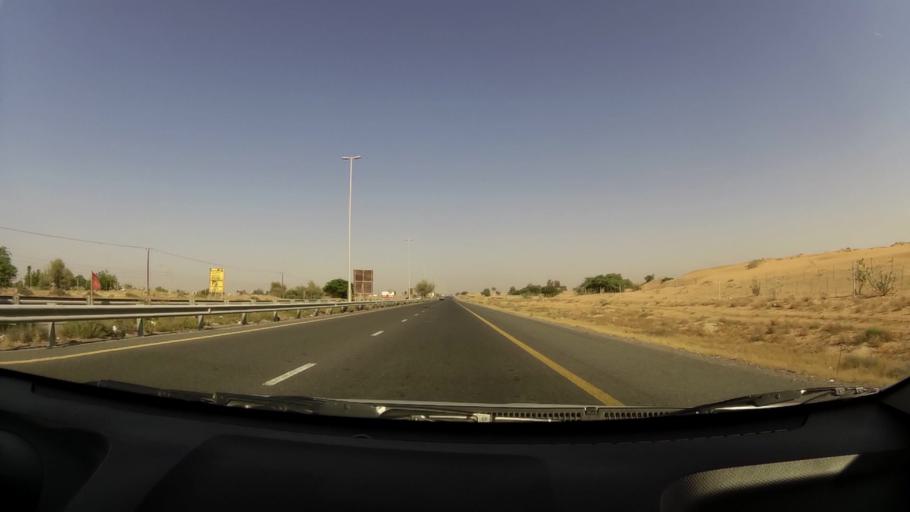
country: AE
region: Umm al Qaywayn
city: Umm al Qaywayn
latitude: 25.4665
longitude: 55.5928
